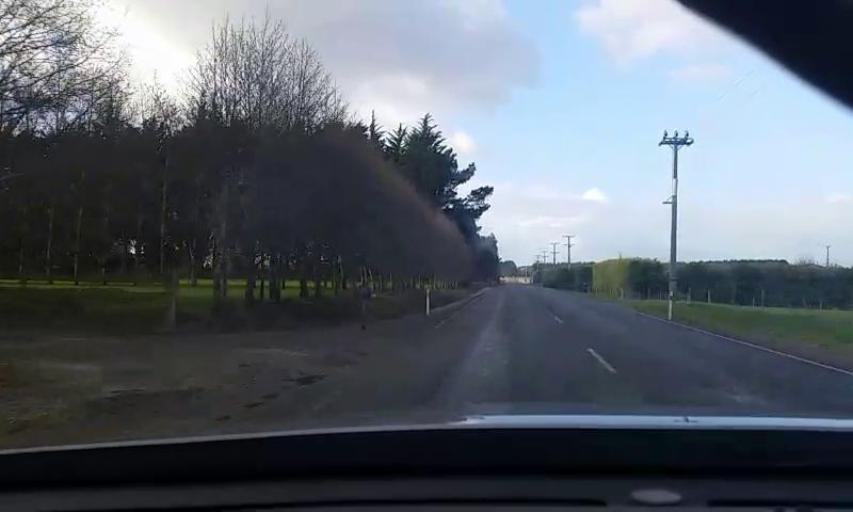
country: NZ
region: Southland
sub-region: Invercargill City
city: Invercargill
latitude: -46.3815
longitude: 168.4445
